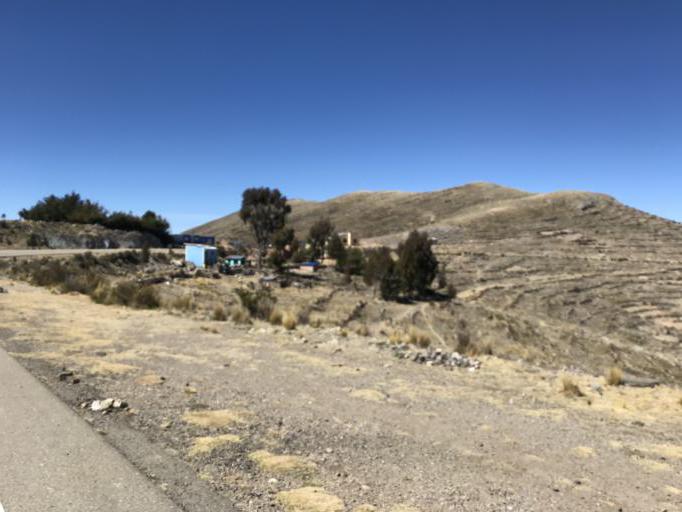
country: BO
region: La Paz
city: San Pedro
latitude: -16.2001
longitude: -68.9044
